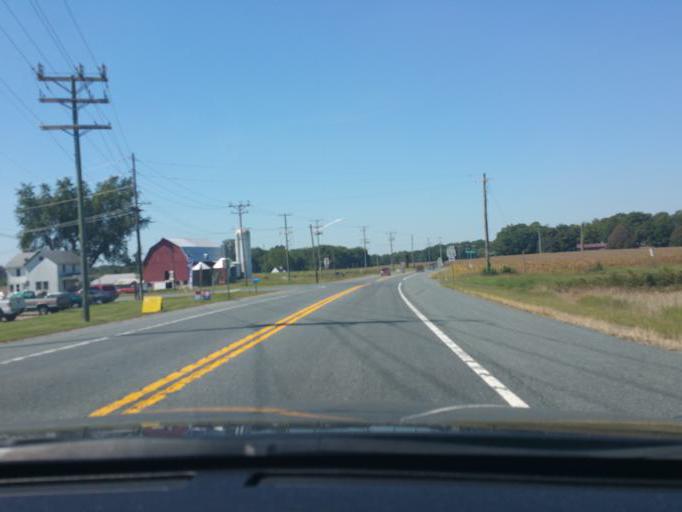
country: US
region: Maryland
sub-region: Harford County
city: Aberdeen
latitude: 39.5723
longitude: -76.1744
